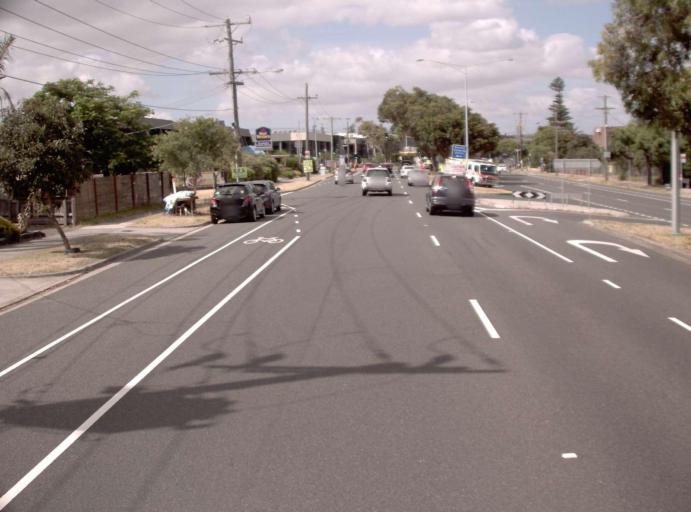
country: AU
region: Victoria
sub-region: Frankston
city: Frankston
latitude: -38.1372
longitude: 145.1239
